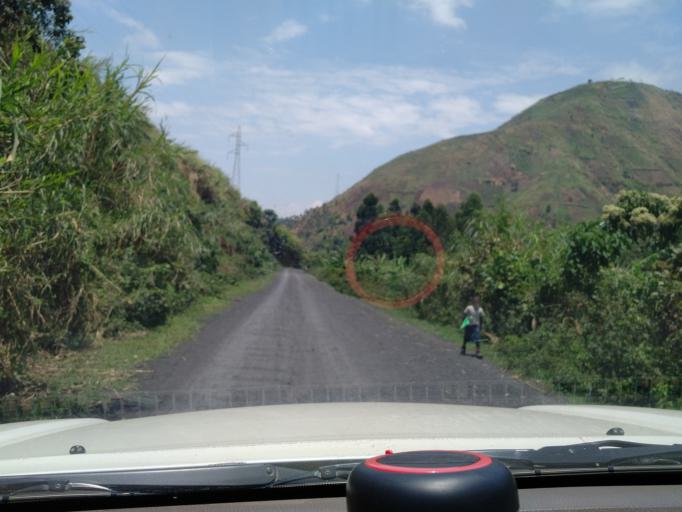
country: CD
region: Nord Kivu
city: Sake
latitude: -1.7657
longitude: 28.9965
